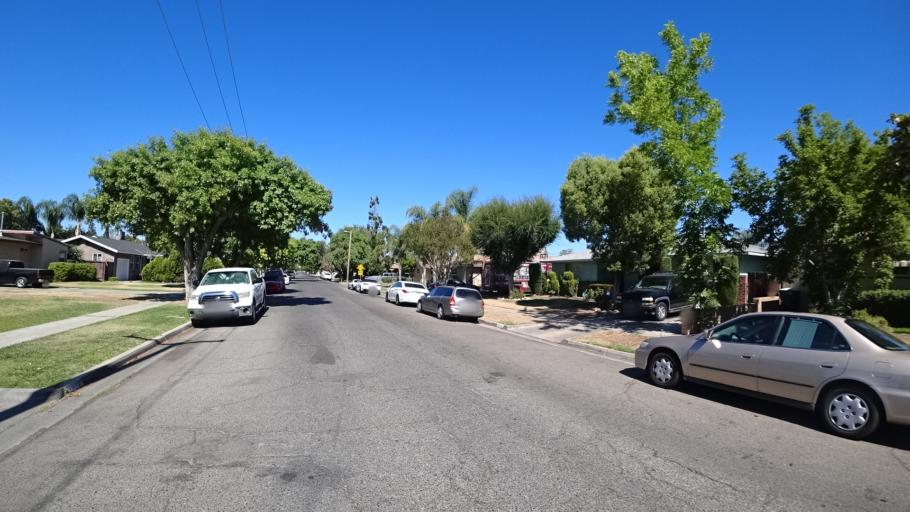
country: US
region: California
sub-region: Fresno County
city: Fresno
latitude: 36.7902
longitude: -119.8289
